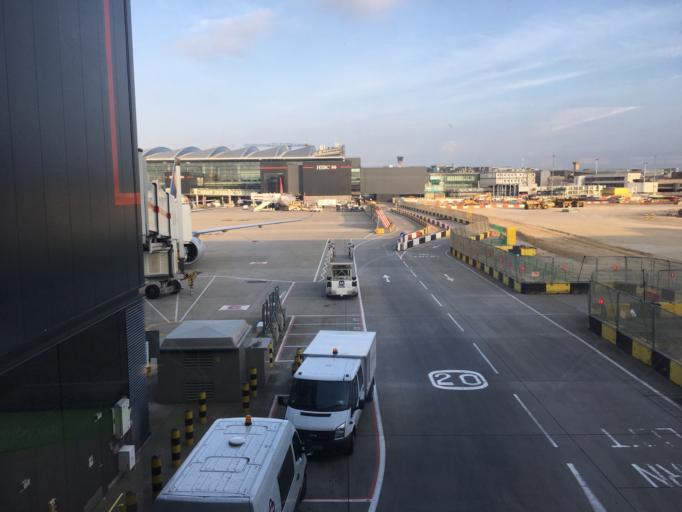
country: GB
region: England
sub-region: Greater London
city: West Drayton
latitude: 51.4705
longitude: -0.4434
